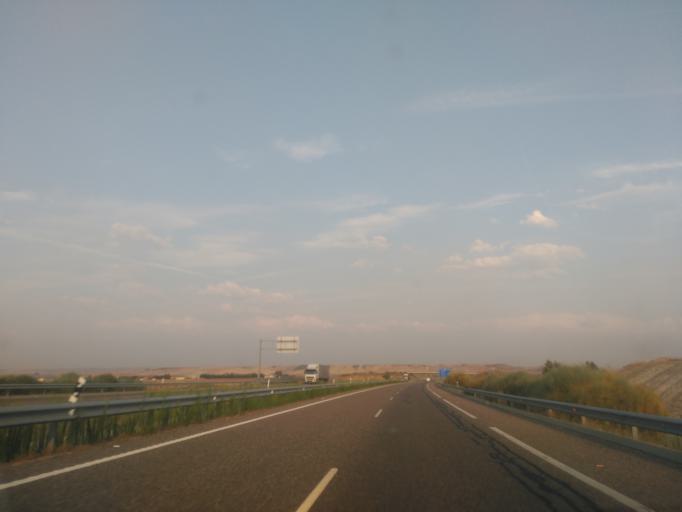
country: ES
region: Castille and Leon
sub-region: Provincia de Zamora
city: Monfarracinos
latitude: 41.5522
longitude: -5.7277
